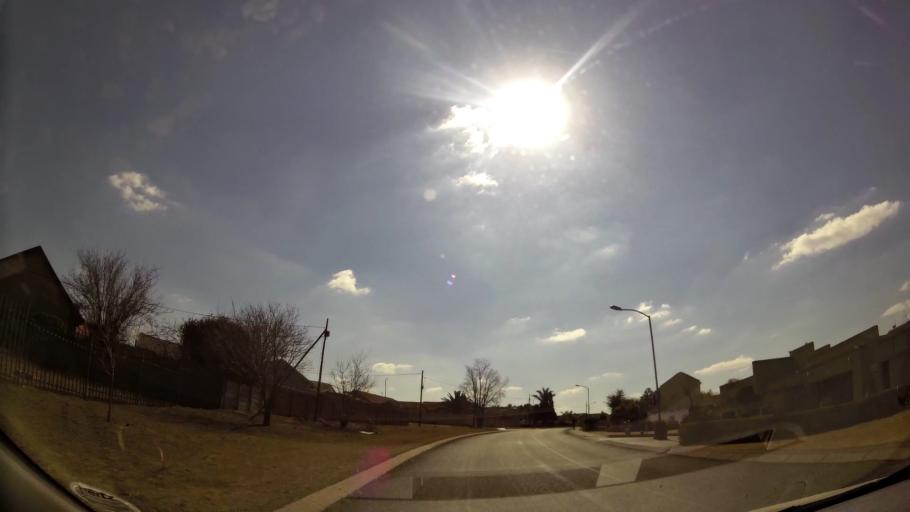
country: ZA
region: Gauteng
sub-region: West Rand District Municipality
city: Randfontein
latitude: -26.1717
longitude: 27.7474
